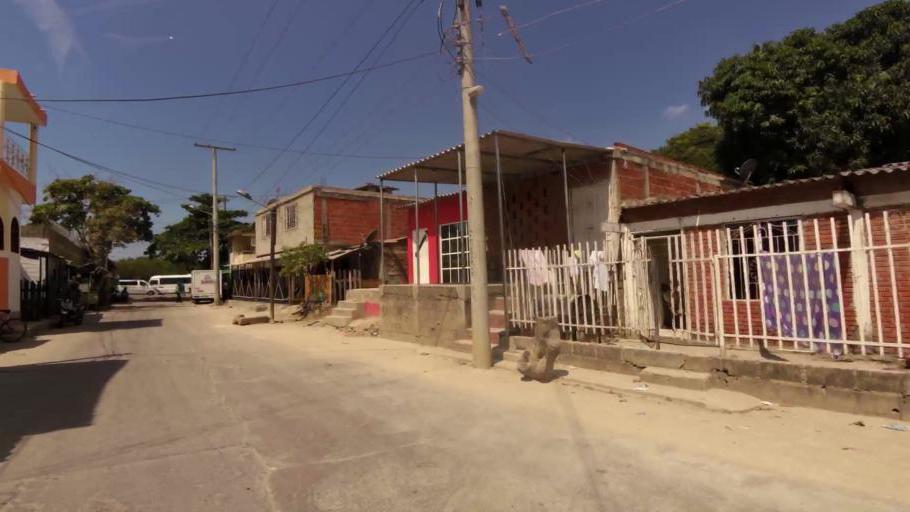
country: CO
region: Bolivar
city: Cartagena
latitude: 10.3457
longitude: -75.4942
